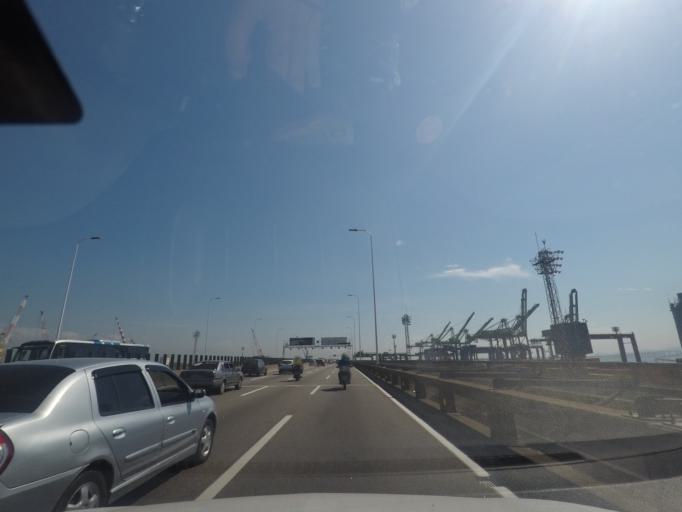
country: BR
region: Rio de Janeiro
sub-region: Rio De Janeiro
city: Rio de Janeiro
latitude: -22.8770
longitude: -43.2097
